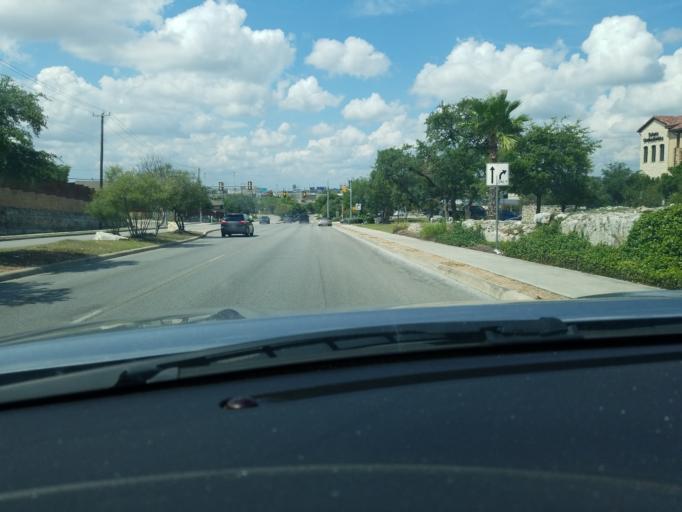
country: US
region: Texas
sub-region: Bexar County
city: Timberwood Park
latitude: 29.6509
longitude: -98.4466
